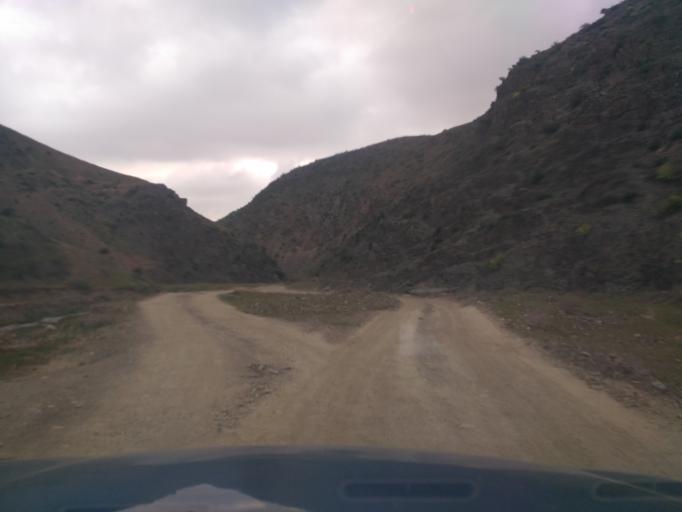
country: UZ
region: Jizzax
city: Zomin
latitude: 39.8528
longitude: 68.3935
